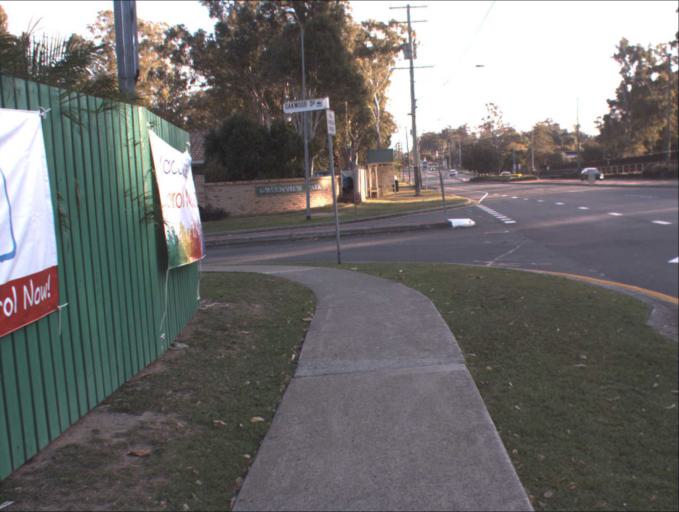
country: AU
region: Queensland
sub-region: Logan
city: Waterford West
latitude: -27.6860
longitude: 153.1075
